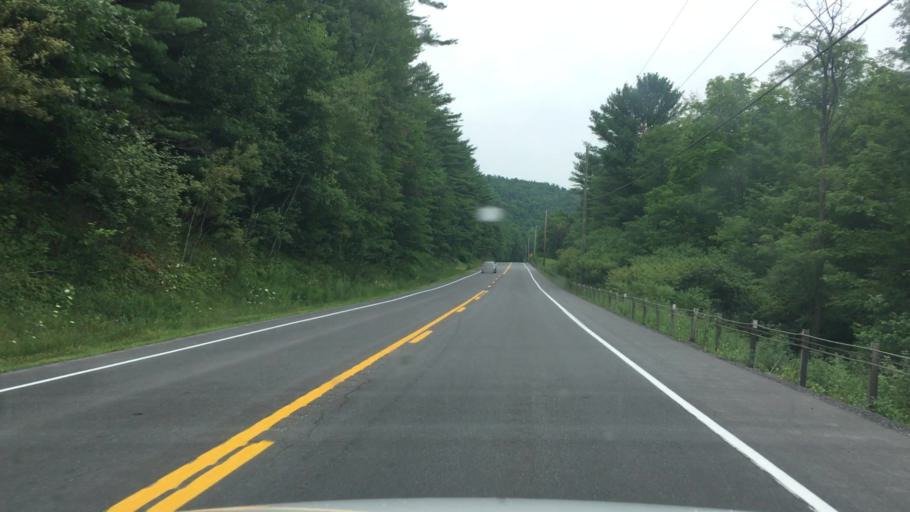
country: US
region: New York
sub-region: Essex County
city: Keeseville
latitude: 44.4708
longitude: -73.5710
